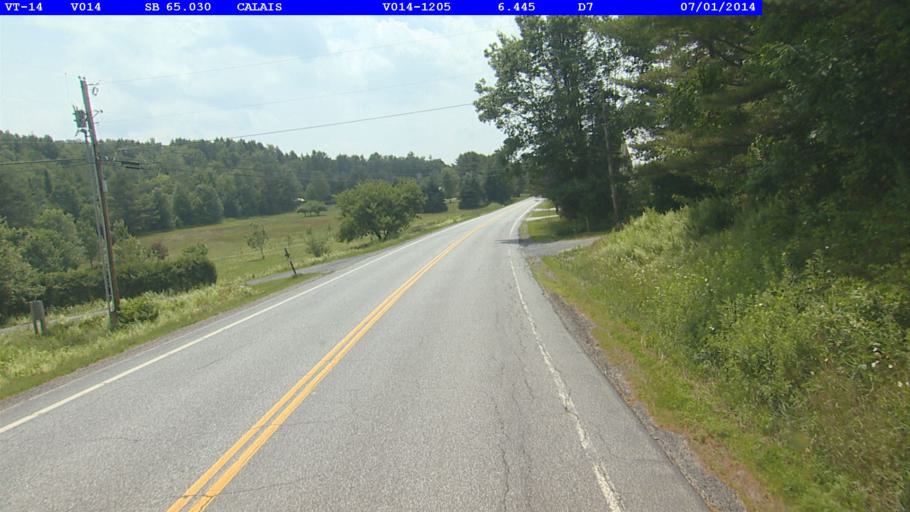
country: US
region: Vermont
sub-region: Caledonia County
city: Hardwick
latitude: 44.3897
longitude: -72.4148
